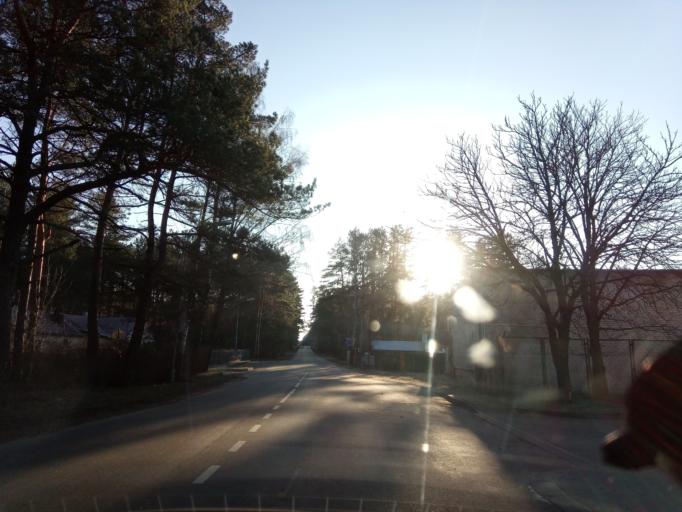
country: LT
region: Alytaus apskritis
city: Druskininkai
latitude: 54.0020
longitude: 23.9814
